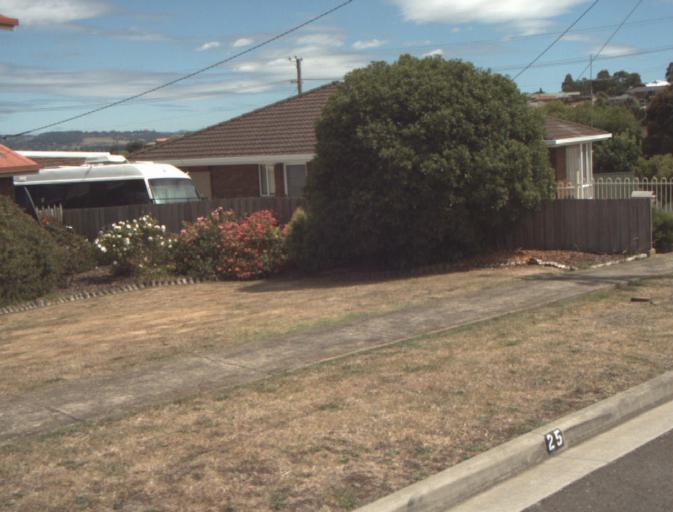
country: AU
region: Tasmania
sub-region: Launceston
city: Mayfield
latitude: -41.3836
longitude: 147.1240
